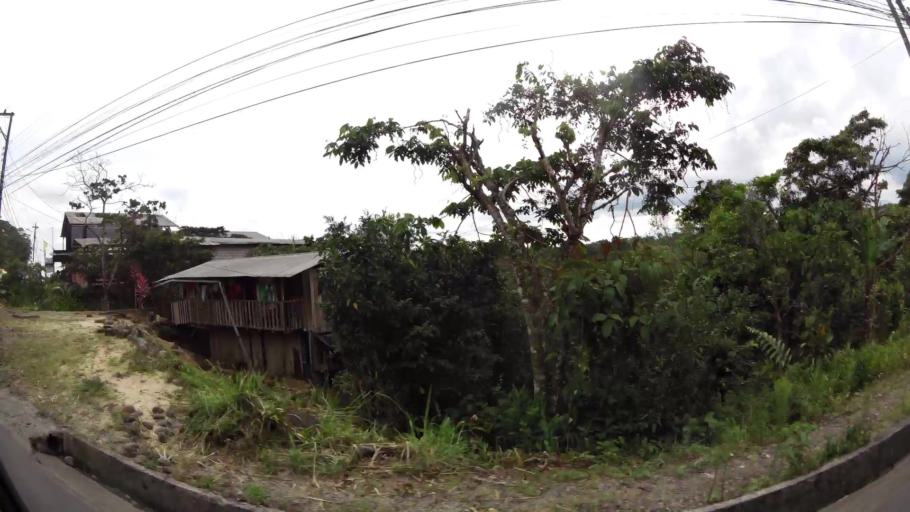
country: EC
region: Pastaza
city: Puyo
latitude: -1.5049
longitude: -78.0368
